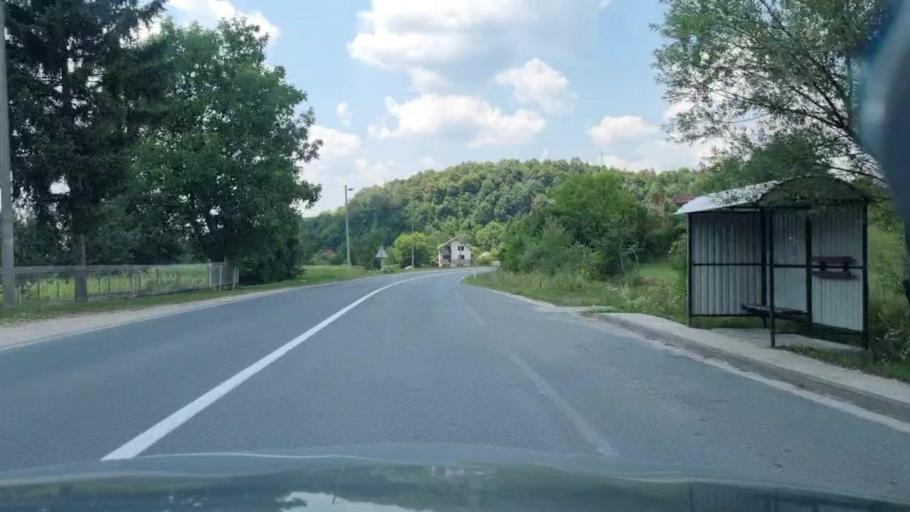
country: BA
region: Federation of Bosnia and Herzegovina
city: Gornja Tuzla
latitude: 44.5318
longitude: 18.7799
